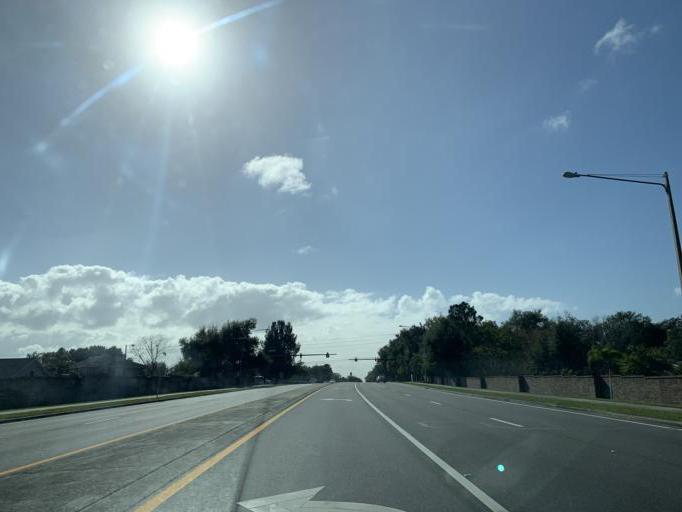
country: US
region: Florida
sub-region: Orange County
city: Clarcona
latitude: 28.6269
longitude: -81.4764
